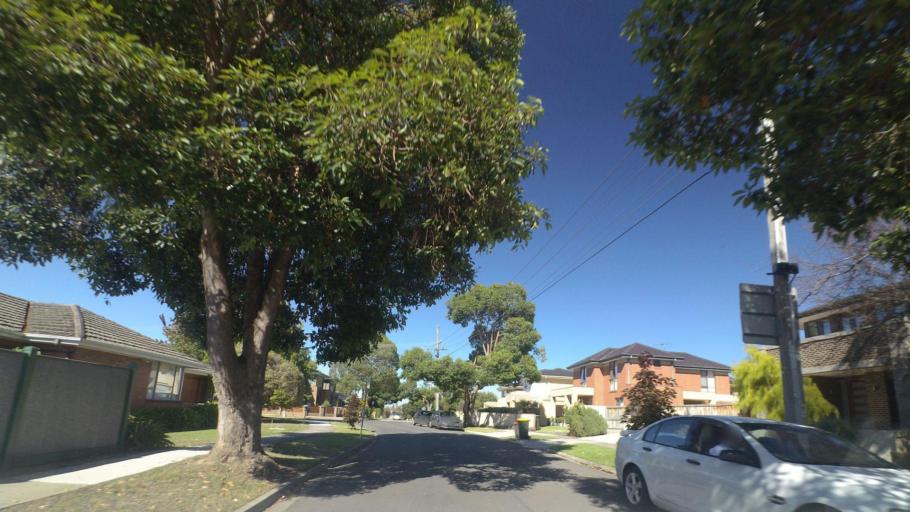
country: AU
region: Victoria
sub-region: Manningham
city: Donvale
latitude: -37.7886
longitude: 145.1675
